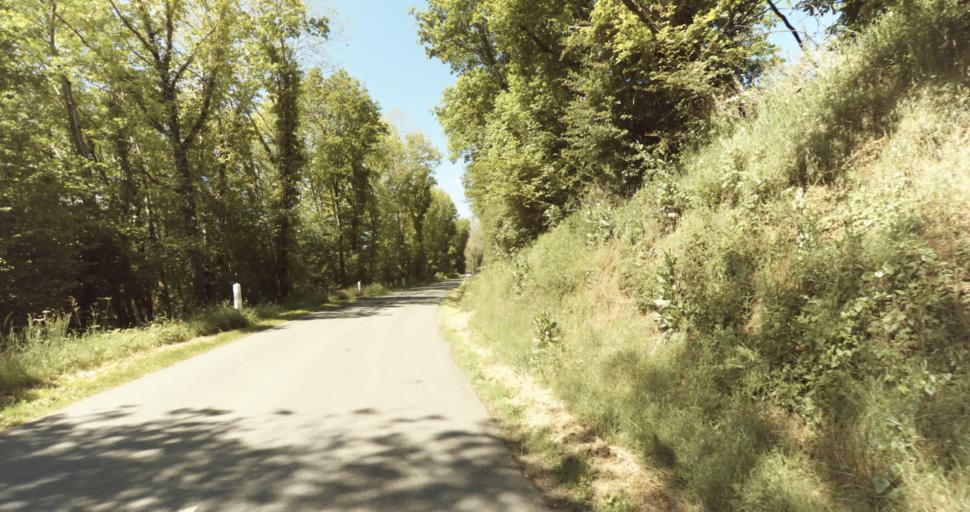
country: FR
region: Limousin
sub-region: Departement de la Haute-Vienne
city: Le Vigen
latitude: 45.7495
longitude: 1.3003
